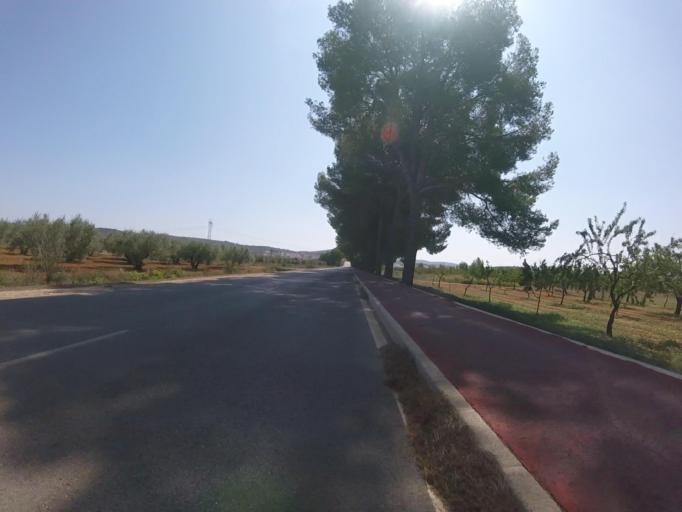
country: ES
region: Valencia
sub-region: Provincia de Castello
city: Cabanes
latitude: 40.1602
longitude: 0.0297
